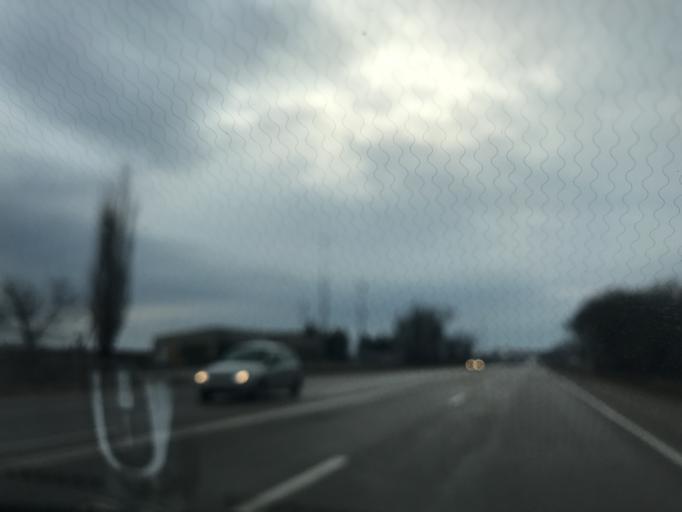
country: RU
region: Krasnodarskiy
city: Tikhoretsk
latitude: 45.8723
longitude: 40.1440
